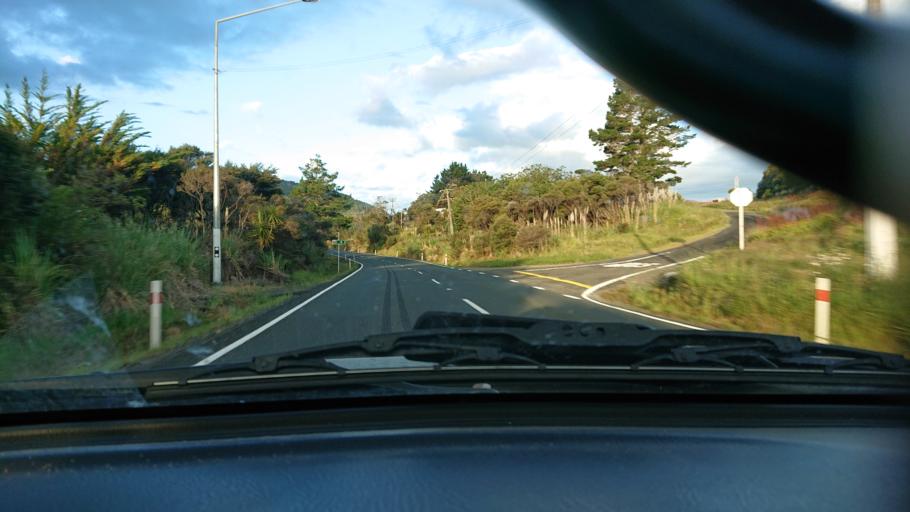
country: NZ
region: Auckland
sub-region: Auckland
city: Parakai
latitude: -36.5099
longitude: 174.4545
